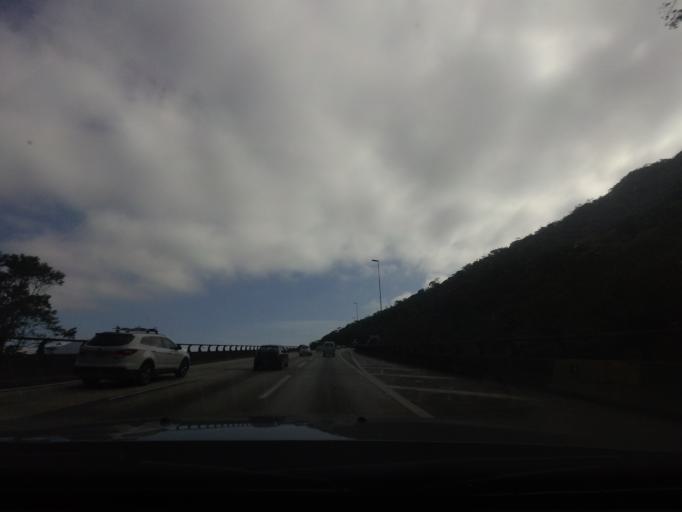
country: BR
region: Sao Paulo
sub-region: Cubatao
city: Cubatao
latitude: -23.9144
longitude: -46.5205
